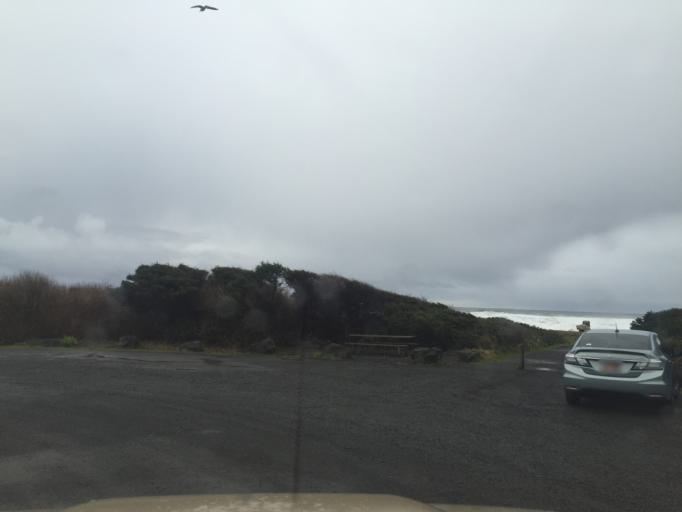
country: US
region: Oregon
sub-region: Lincoln County
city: Waldport
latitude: 44.3221
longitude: -124.1056
